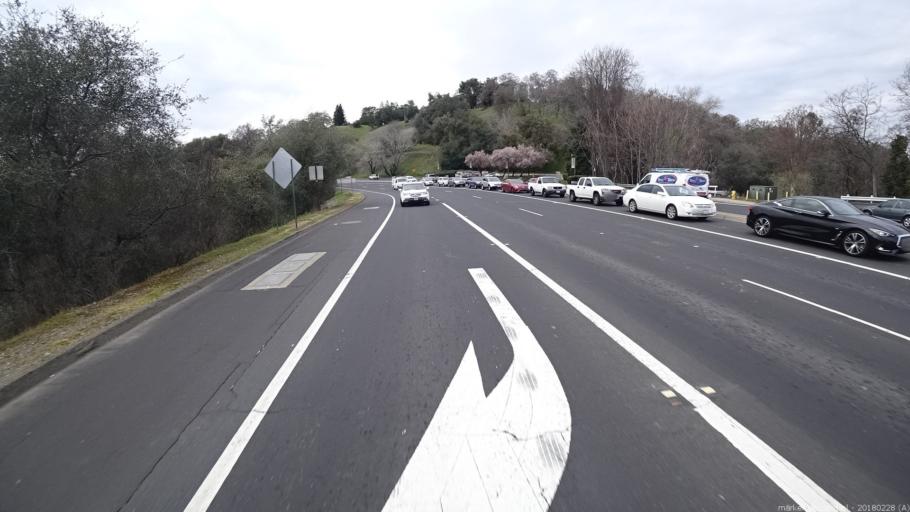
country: US
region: California
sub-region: Sacramento County
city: Folsom
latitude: 38.6843
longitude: -121.1798
